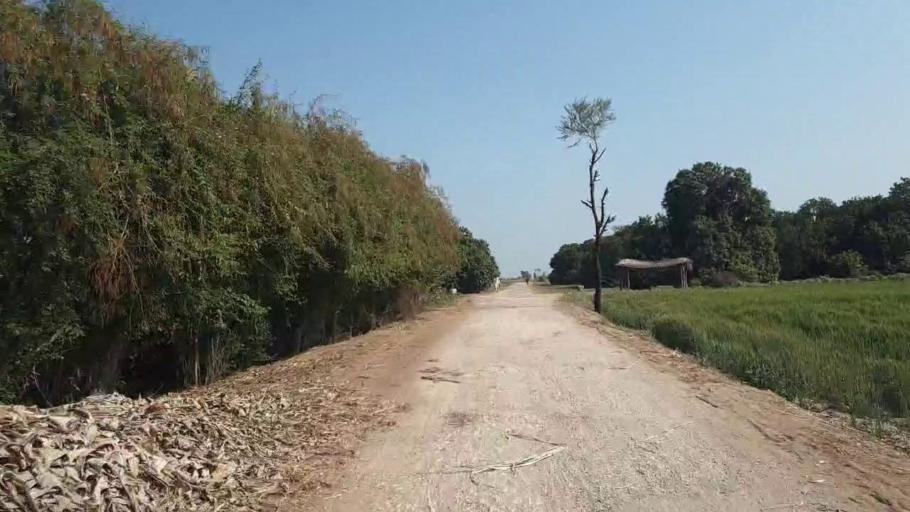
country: PK
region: Sindh
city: Bhit Shah
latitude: 25.9497
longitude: 68.4755
